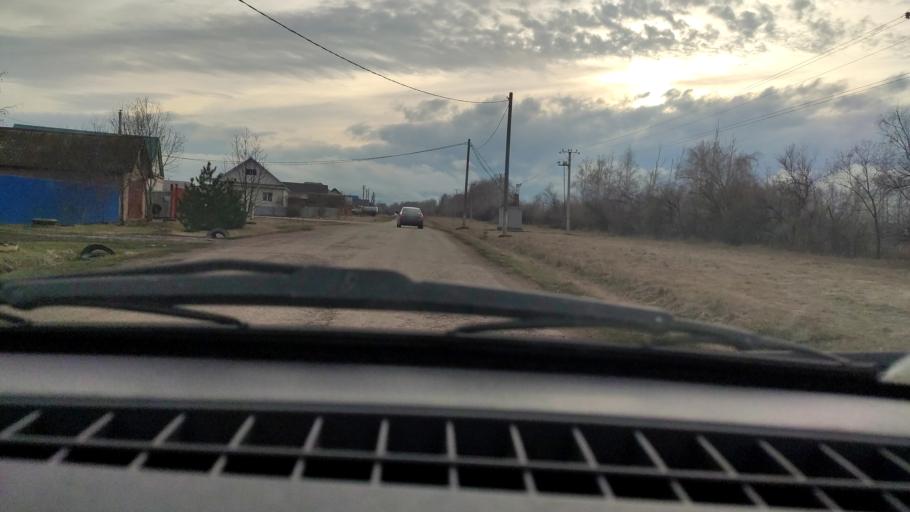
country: RU
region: Bashkortostan
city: Davlekanovo
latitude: 54.2340
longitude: 55.0284
